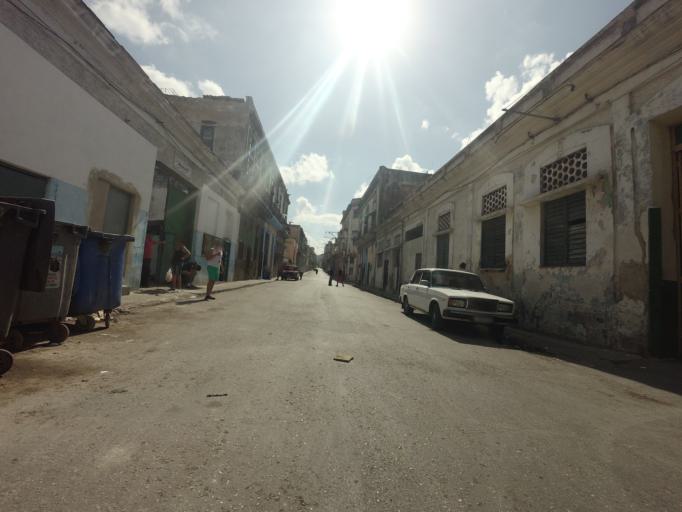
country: CU
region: La Habana
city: Centro Habana
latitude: 23.1396
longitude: -82.3730
